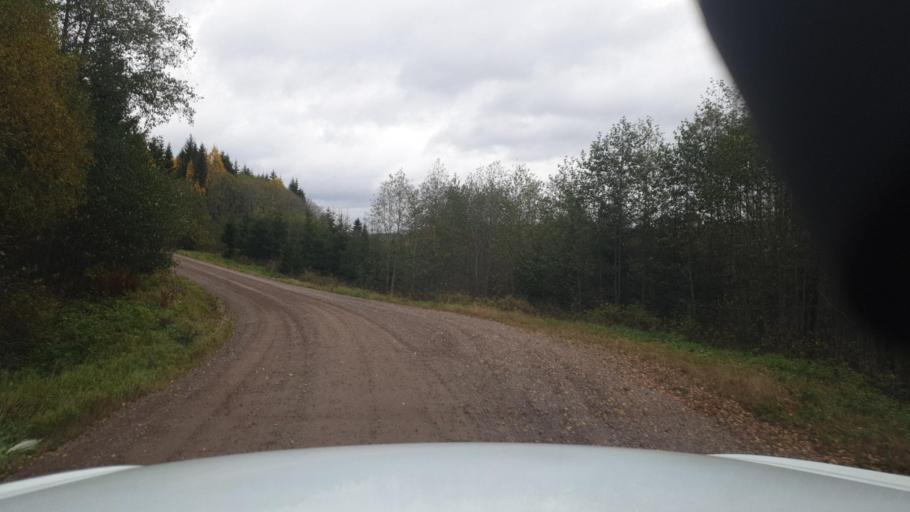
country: SE
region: Vaermland
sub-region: Arvika Kommun
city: Arvika
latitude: 60.0072
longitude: 12.6579
